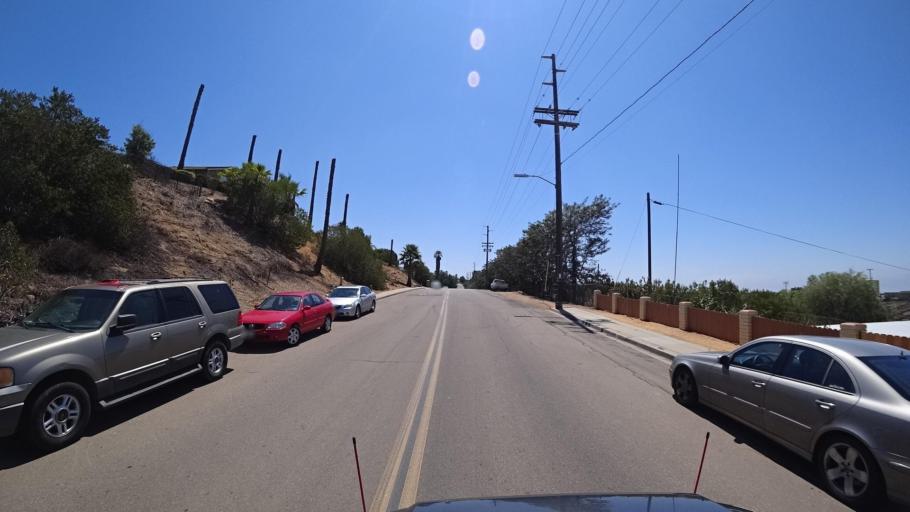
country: US
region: California
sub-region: San Diego County
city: Fallbrook
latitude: 33.3651
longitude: -117.2580
